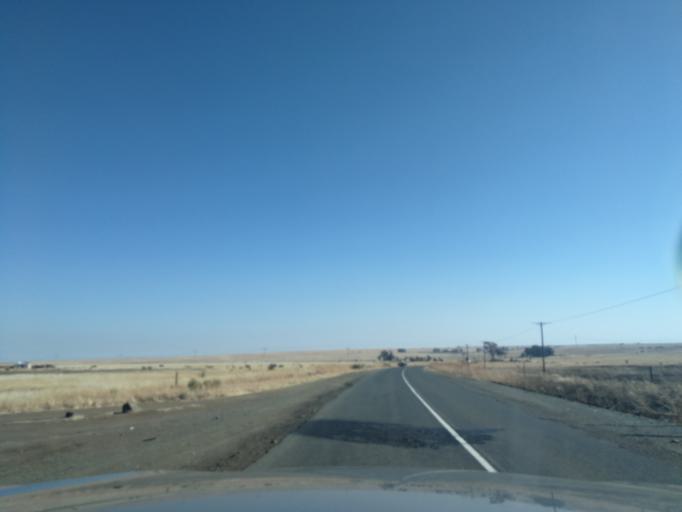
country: ZA
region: Orange Free State
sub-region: Thabo Mofutsanyana District Municipality
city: Senekal
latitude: -27.9383
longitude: 27.5546
